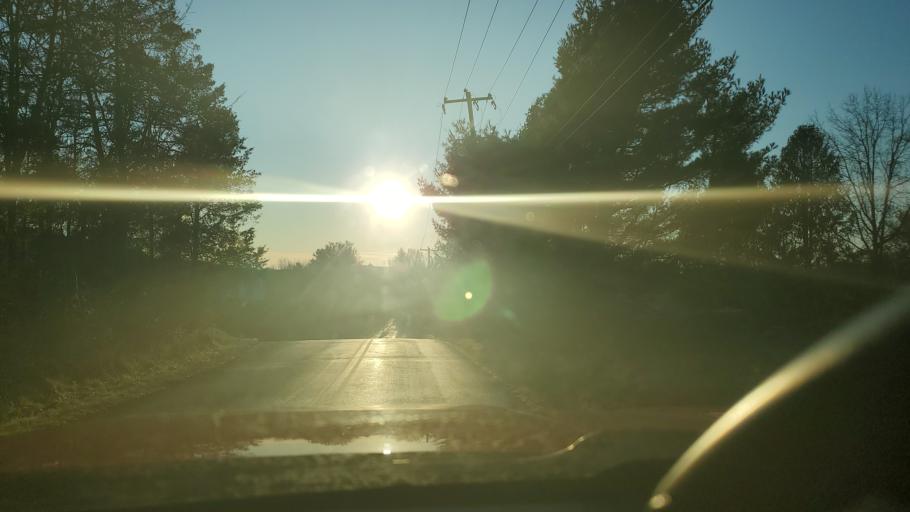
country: US
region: Pennsylvania
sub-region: Montgomery County
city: Woxall
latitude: 40.3066
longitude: -75.4909
